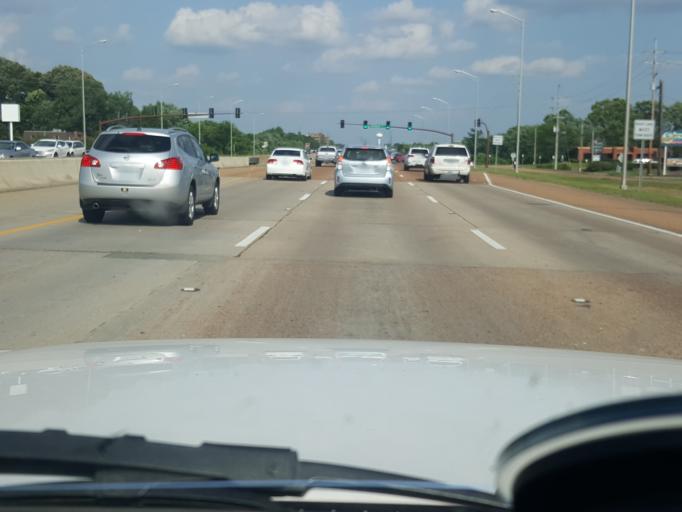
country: US
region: Mississippi
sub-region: Rankin County
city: Flowood
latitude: 32.3330
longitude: -90.1348
